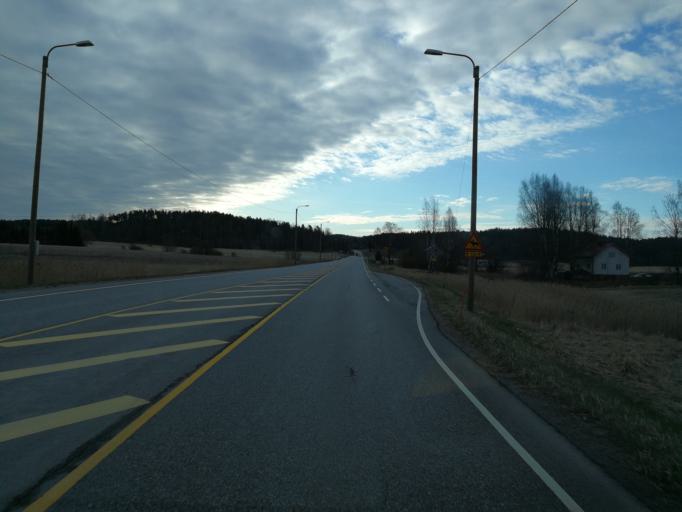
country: FI
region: Varsinais-Suomi
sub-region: Turku
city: Piikkioe
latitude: 60.4346
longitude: 22.5882
